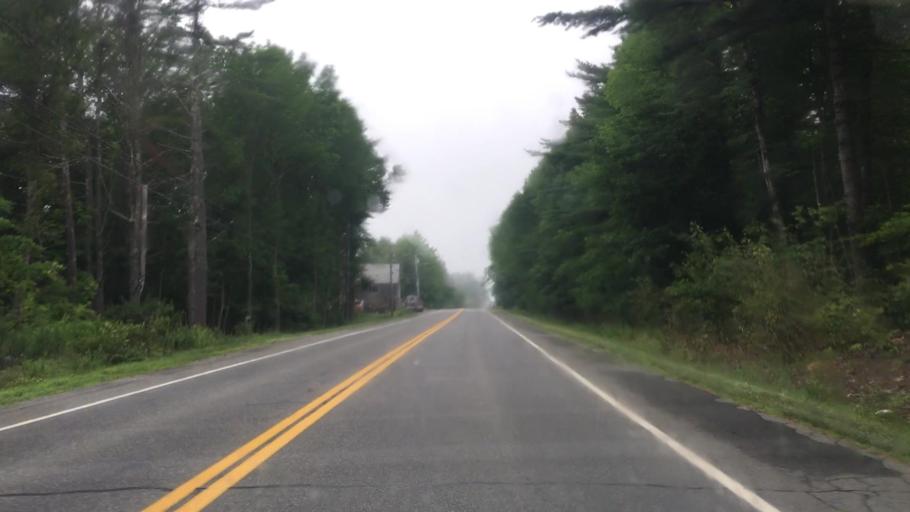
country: US
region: Maine
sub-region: Lincoln County
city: Wiscasset
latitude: 44.0587
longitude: -69.6864
